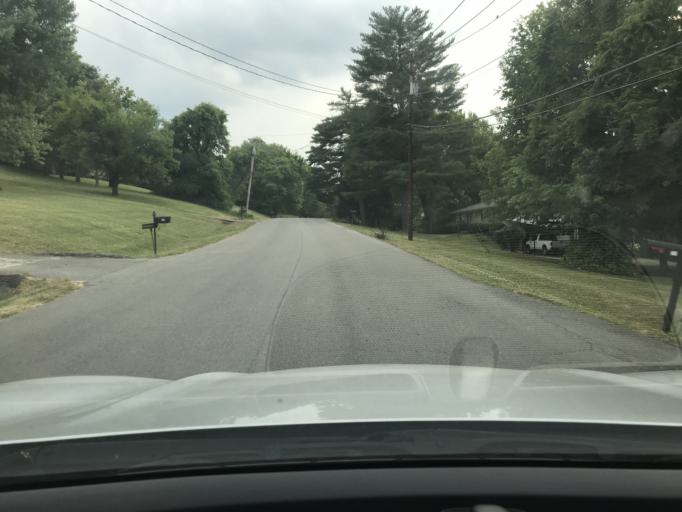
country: US
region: Tennessee
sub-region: Davidson County
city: Goodlettsville
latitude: 36.3137
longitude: -86.7187
